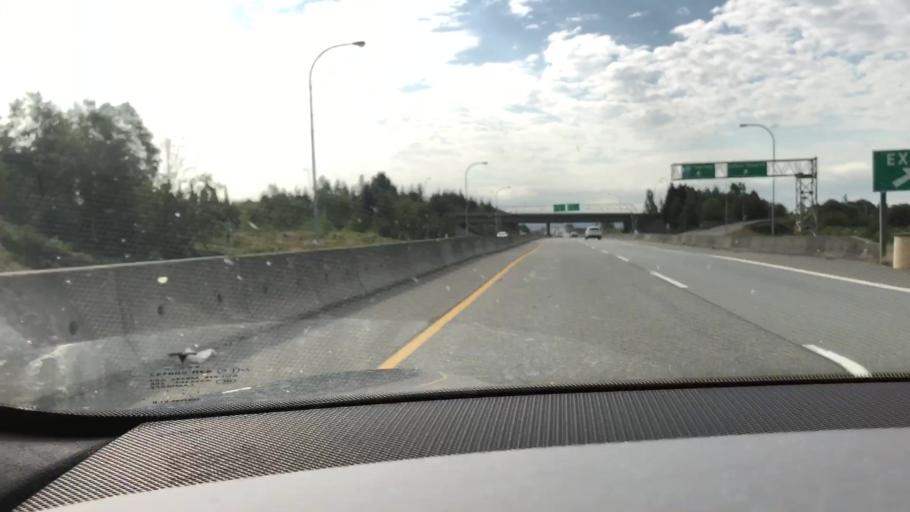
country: CA
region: British Columbia
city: Delta
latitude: 49.1049
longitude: -122.9019
